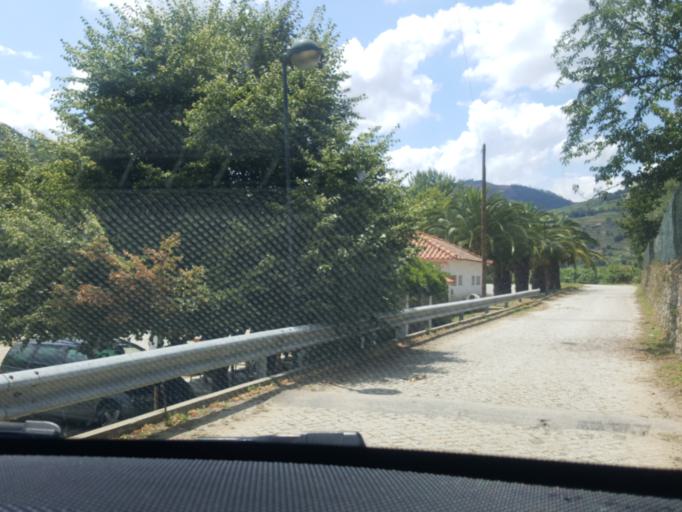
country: PT
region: Vila Real
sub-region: Mesao Frio
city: Mesao Frio
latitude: 41.1596
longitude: -7.8648
